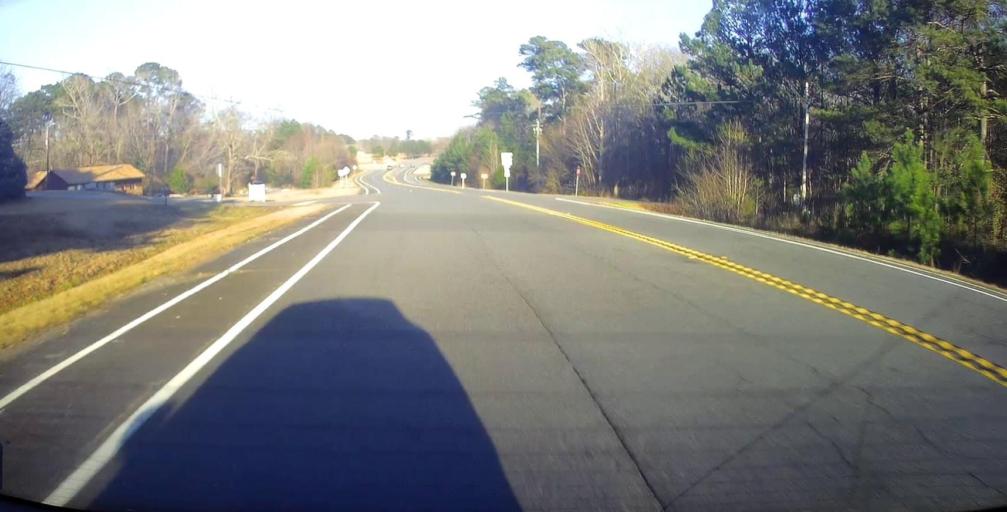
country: US
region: Georgia
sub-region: Harris County
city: Pine Mountain
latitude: 32.8512
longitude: -84.8707
